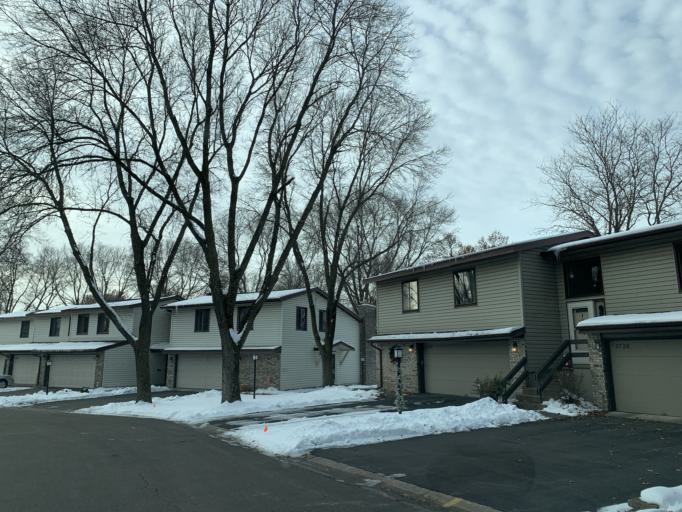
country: US
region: Minnesota
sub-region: Scott County
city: Savage
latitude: 44.8292
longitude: -93.3560
